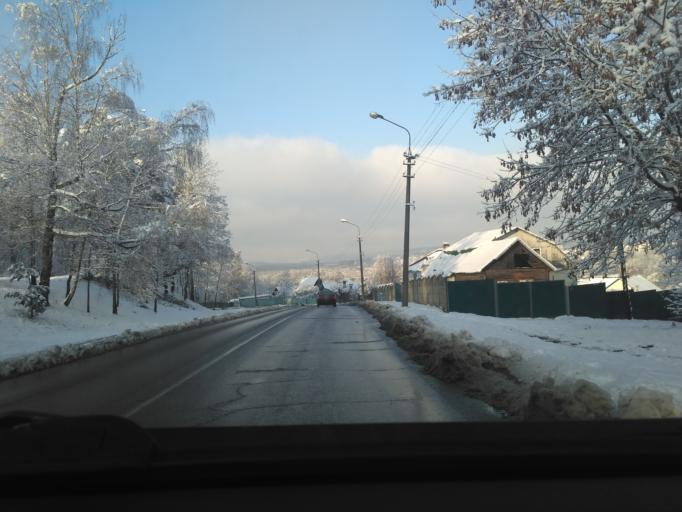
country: BY
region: Minsk
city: Horad Barysaw
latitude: 54.2322
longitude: 28.5006
